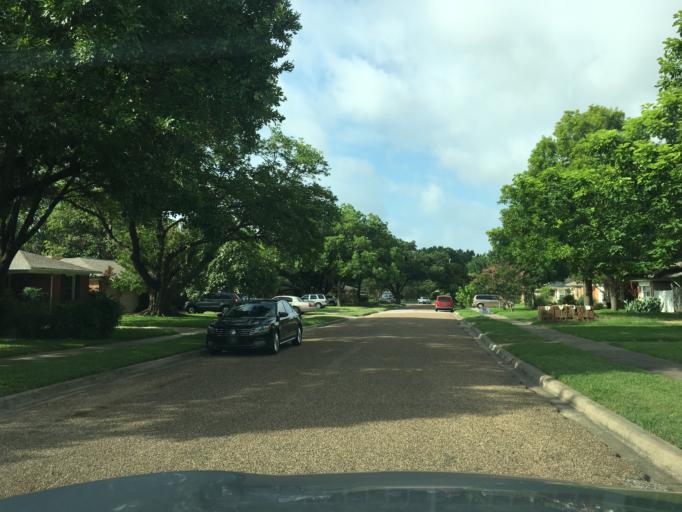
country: US
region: Texas
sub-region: Dallas County
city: Richardson
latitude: 32.9469
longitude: -96.7243
